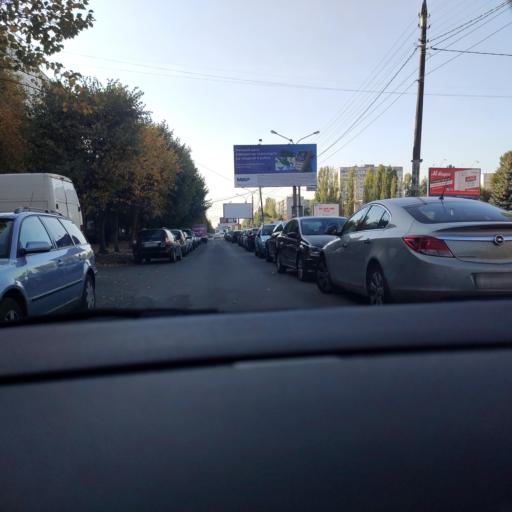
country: RU
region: Voronezj
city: Voronezh
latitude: 51.7066
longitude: 39.1764
